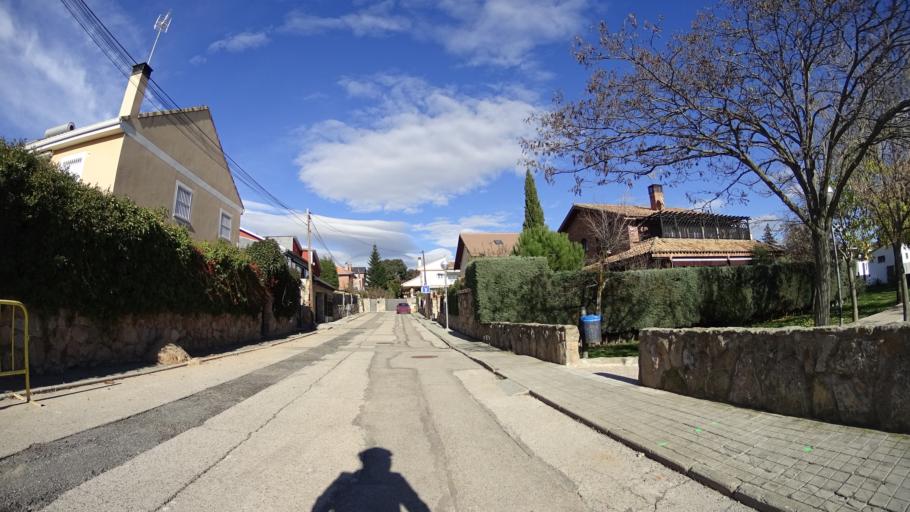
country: ES
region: Madrid
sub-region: Provincia de Madrid
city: Galapagar
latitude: 40.5793
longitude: -4.0199
